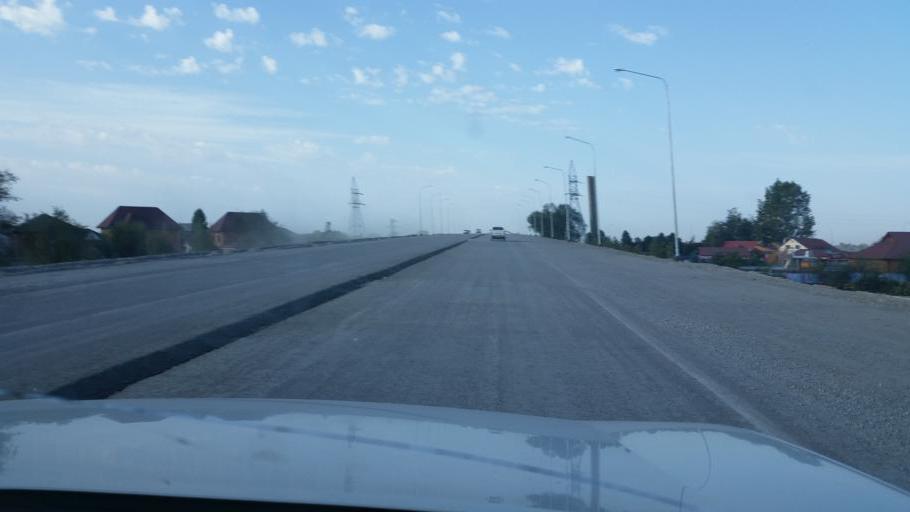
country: KZ
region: Almaty Oblysy
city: Energeticheskiy
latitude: 43.4428
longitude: 76.9926
